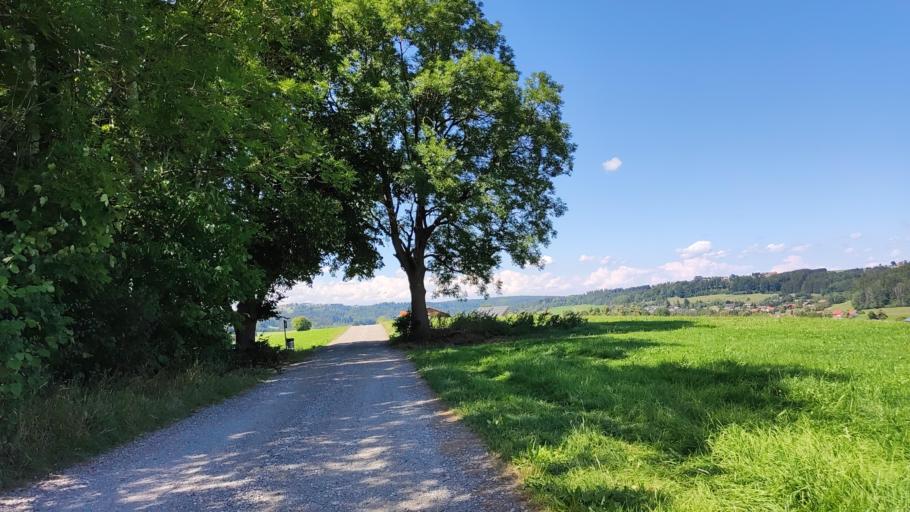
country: DE
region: Bavaria
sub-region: Swabia
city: Obergunzburg
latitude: 47.8402
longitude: 10.4308
